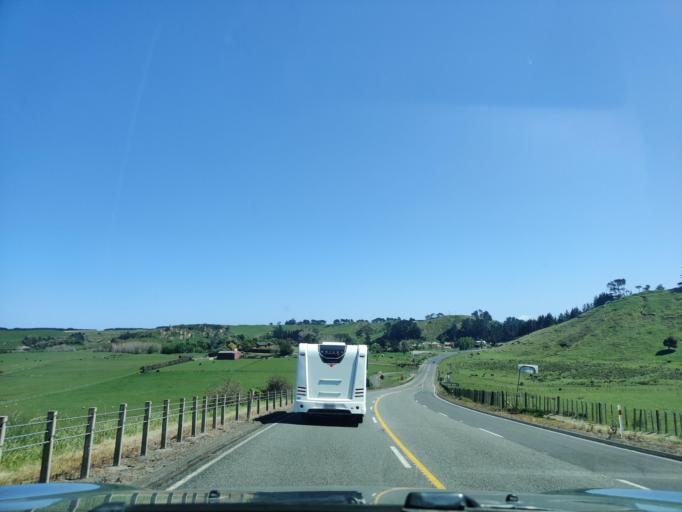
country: NZ
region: Taranaki
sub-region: South Taranaki District
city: Patea
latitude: -39.8111
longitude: 174.7421
